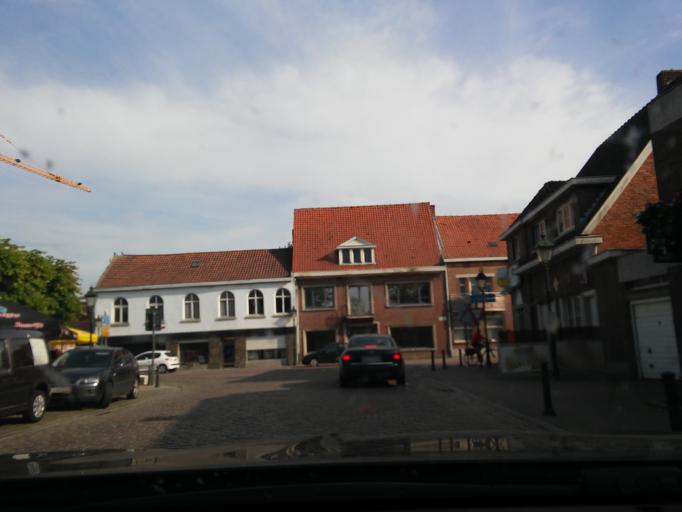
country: BE
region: Flanders
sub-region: Provincie Oost-Vlaanderen
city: Kaprijke
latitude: 51.2301
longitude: 3.6777
